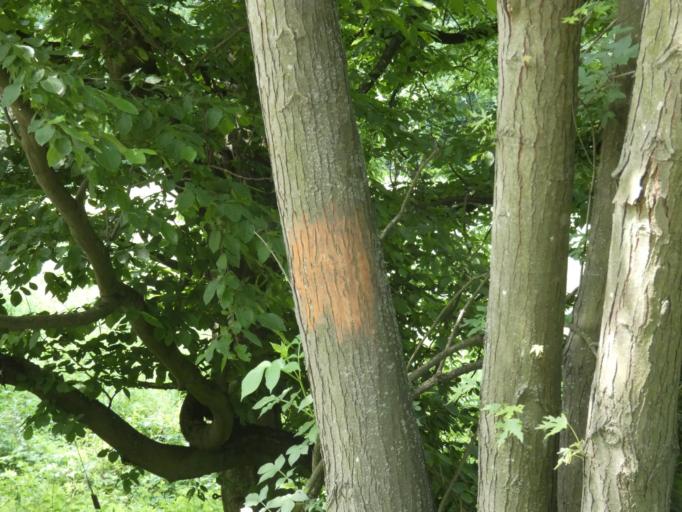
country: HU
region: Pest
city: Szob
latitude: 47.8502
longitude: 18.8494
